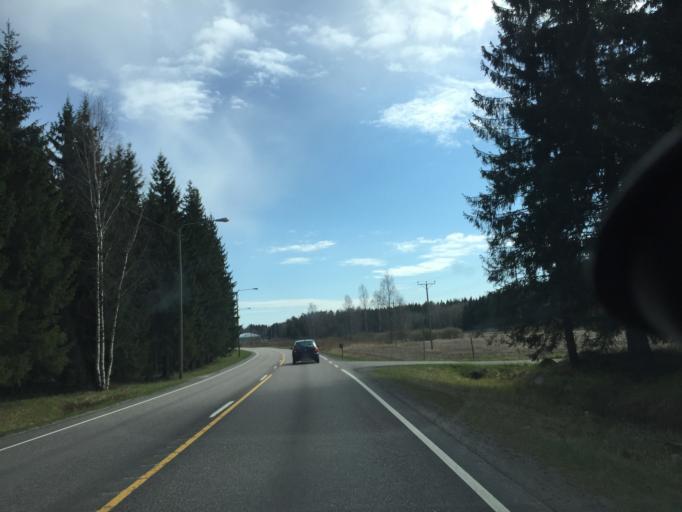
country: FI
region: Uusimaa
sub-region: Raaseporin
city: Ekenaes
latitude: 60.0023
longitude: 23.4024
